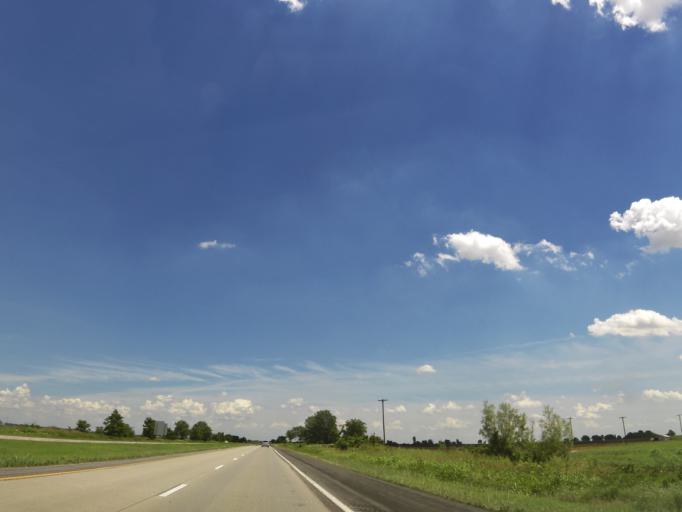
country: US
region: Missouri
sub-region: Pemiscot County
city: Hayti
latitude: 36.1964
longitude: -89.7235
